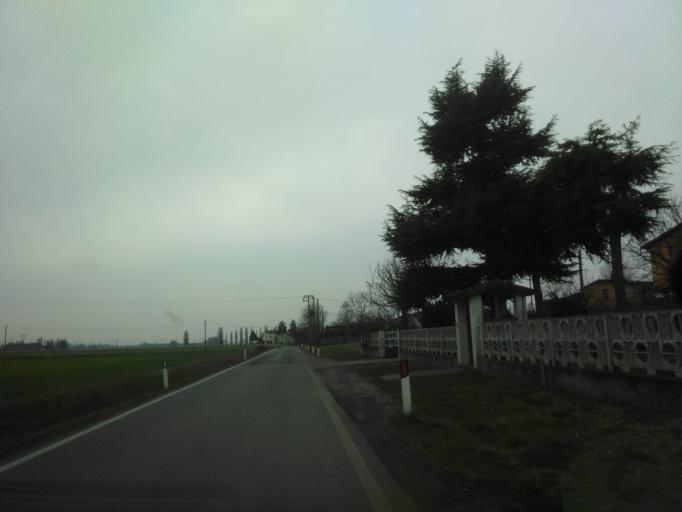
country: IT
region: Lombardy
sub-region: Provincia di Brescia
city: Poncarale
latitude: 45.4473
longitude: 10.1642
